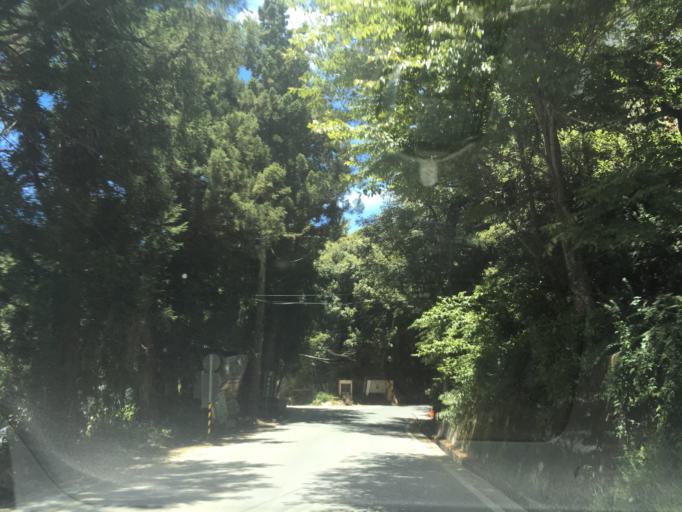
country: TW
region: Taiwan
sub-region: Nantou
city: Puli
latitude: 24.2498
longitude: 121.2528
